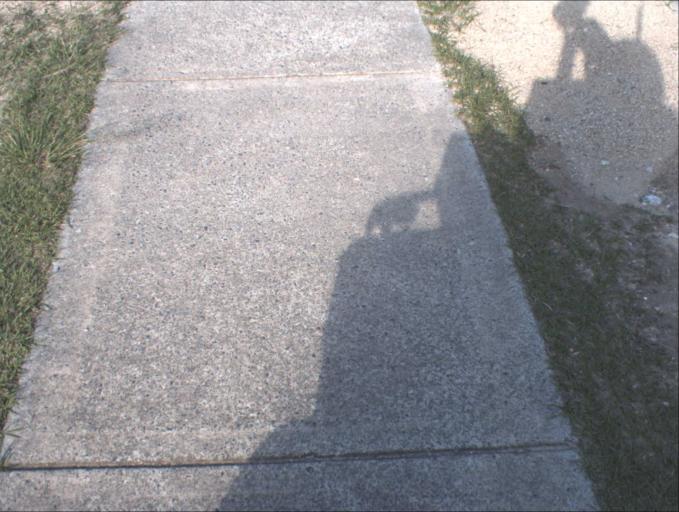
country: AU
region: Queensland
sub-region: Logan
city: Logan Reserve
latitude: -27.6884
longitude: 153.0822
